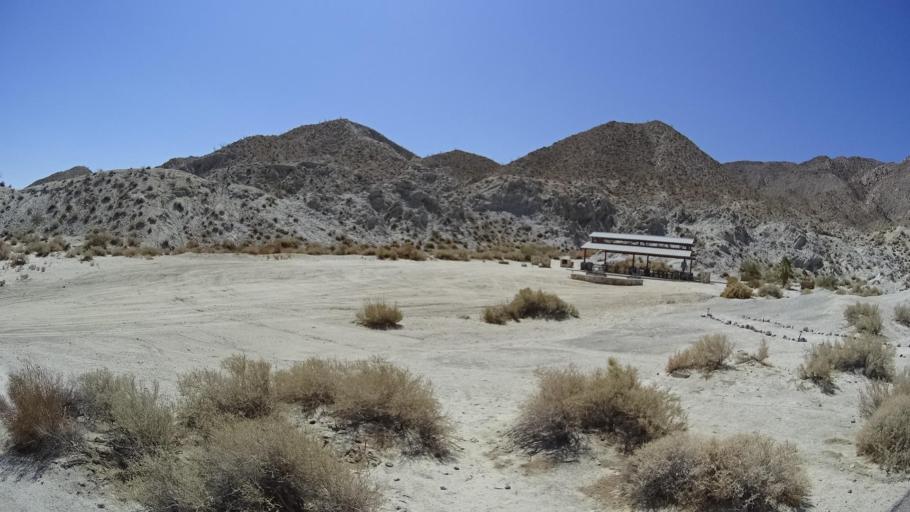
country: US
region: California
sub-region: San Diego County
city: Pine Valley
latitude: 32.9487
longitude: -116.3018
